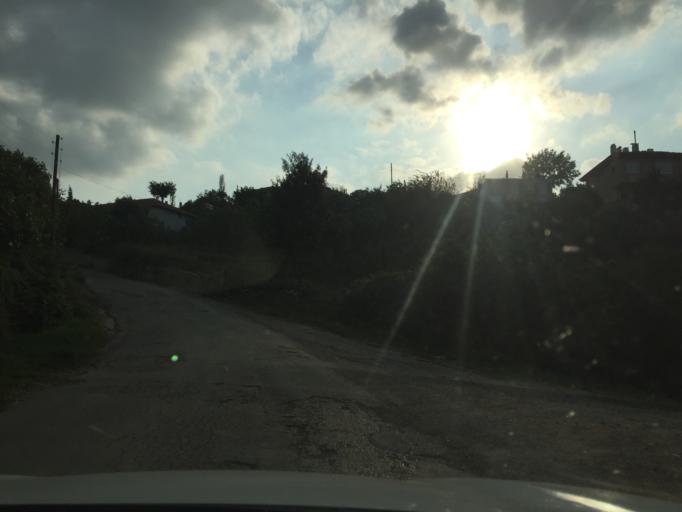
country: TR
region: Balikesir
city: Gonen
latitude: 40.0509
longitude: 27.5853
